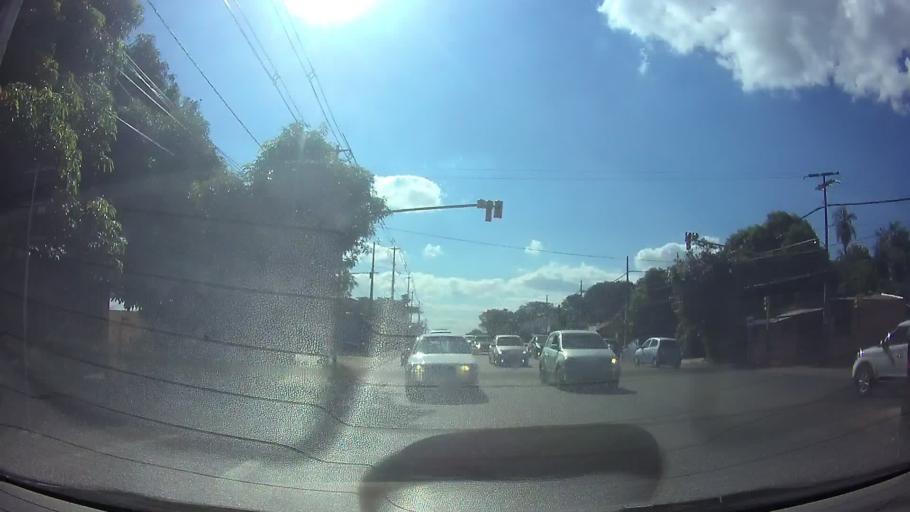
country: PY
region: Central
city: Itaugua
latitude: -25.3991
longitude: -57.3283
